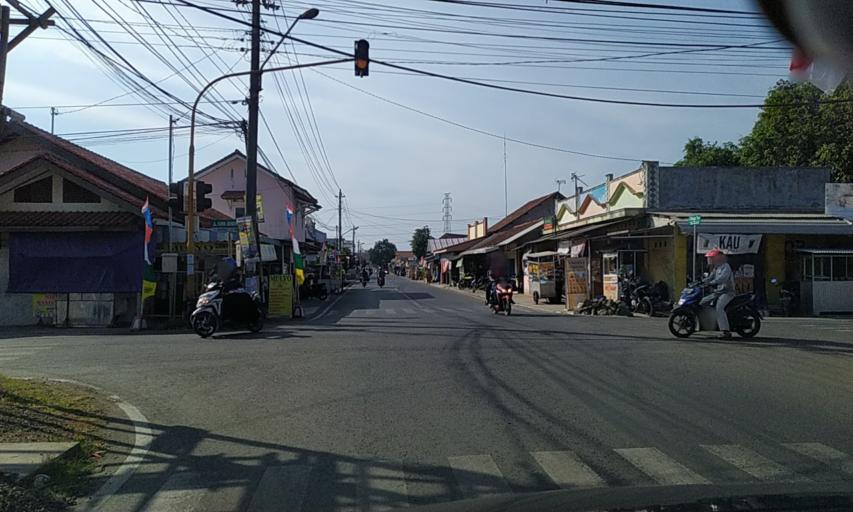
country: ID
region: Central Java
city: Rejanegara
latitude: -7.6728
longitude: 109.0518
